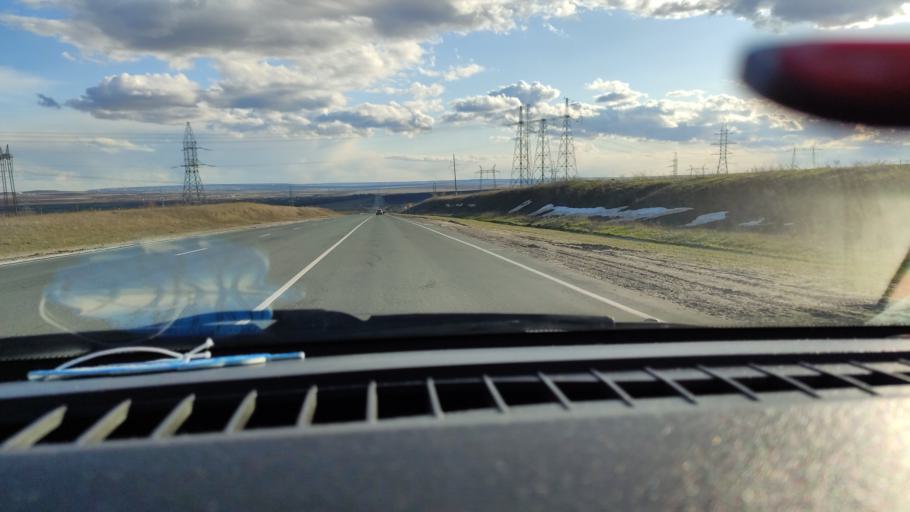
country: RU
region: Saratov
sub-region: Saratovskiy Rayon
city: Saratov
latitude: 51.7637
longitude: 46.0756
